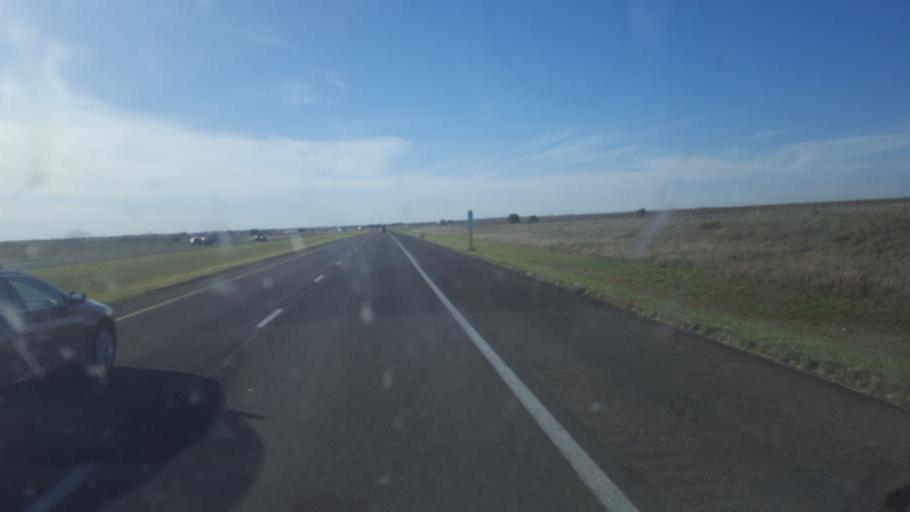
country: US
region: Kansas
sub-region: Ellis County
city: Ellis
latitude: 38.9475
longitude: -99.5155
